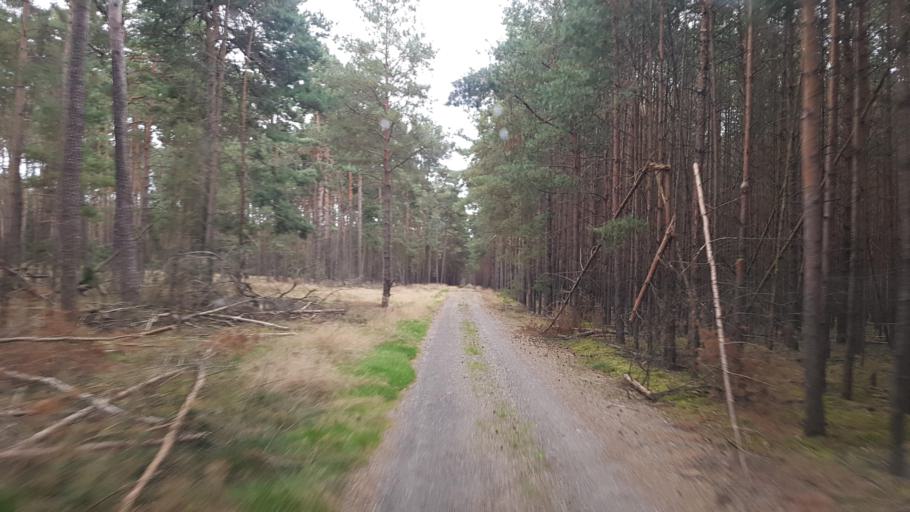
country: DE
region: Brandenburg
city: Sonnewalde
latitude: 51.7403
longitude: 13.6562
